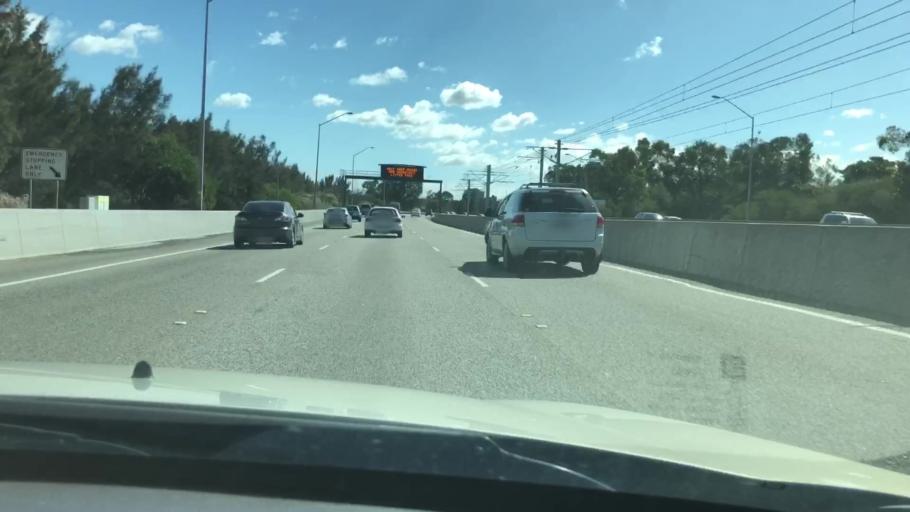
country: AU
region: Western Australia
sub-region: South Perth
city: Manning
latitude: -32.0239
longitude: 115.8590
